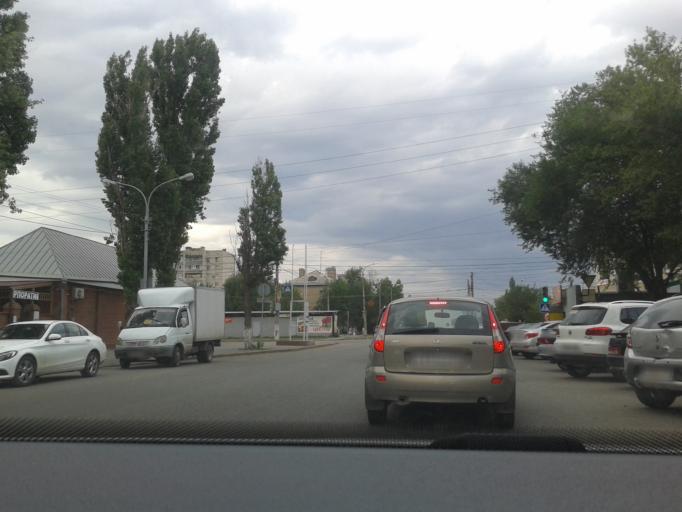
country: RU
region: Volgograd
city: Gorodishche
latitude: 48.7665
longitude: 44.4782
